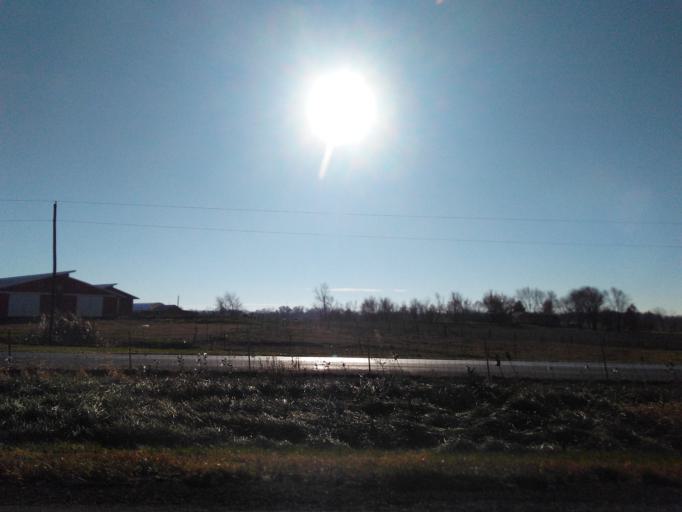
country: US
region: Illinois
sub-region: Madison County
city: Highland
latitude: 38.7932
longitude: -89.6141
